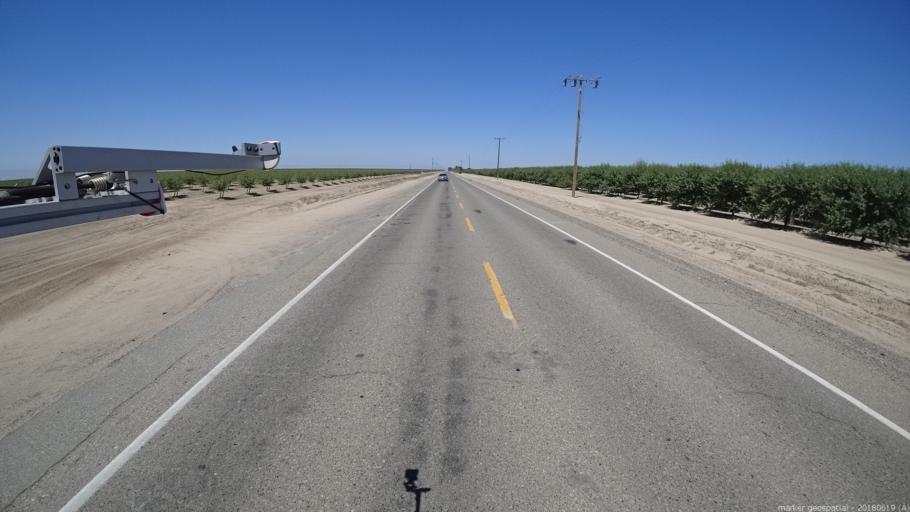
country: US
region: California
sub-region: Fresno County
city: Mendota
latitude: 36.8510
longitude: -120.2747
